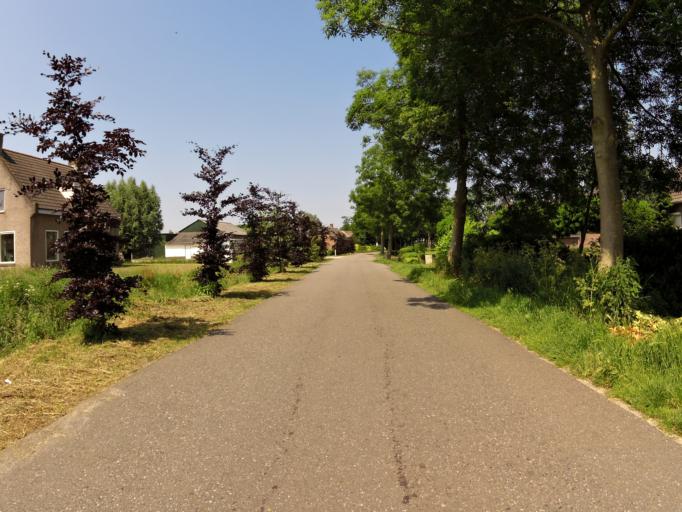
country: NL
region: North Brabant
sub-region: Gemeente Boxtel
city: Boxtel
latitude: 51.6118
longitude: 5.3470
